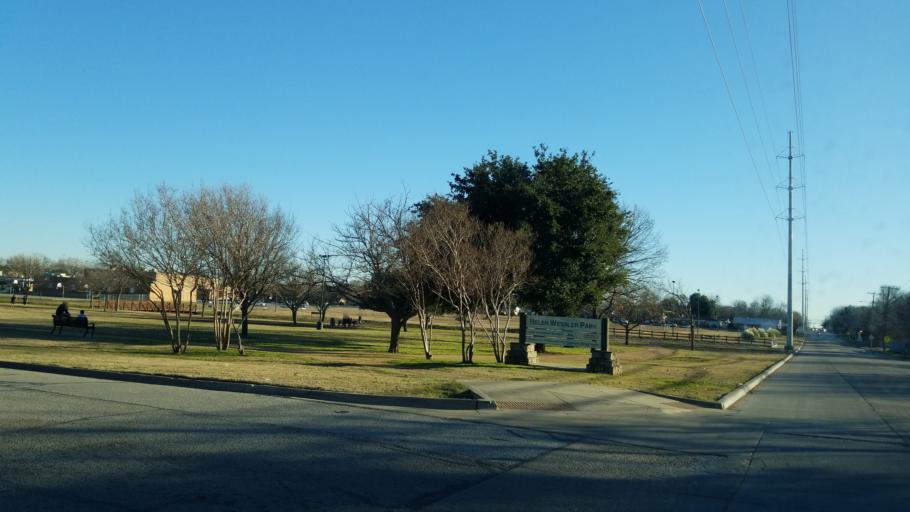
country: US
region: Texas
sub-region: Tarrant County
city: Arlington
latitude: 32.7281
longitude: -97.0717
